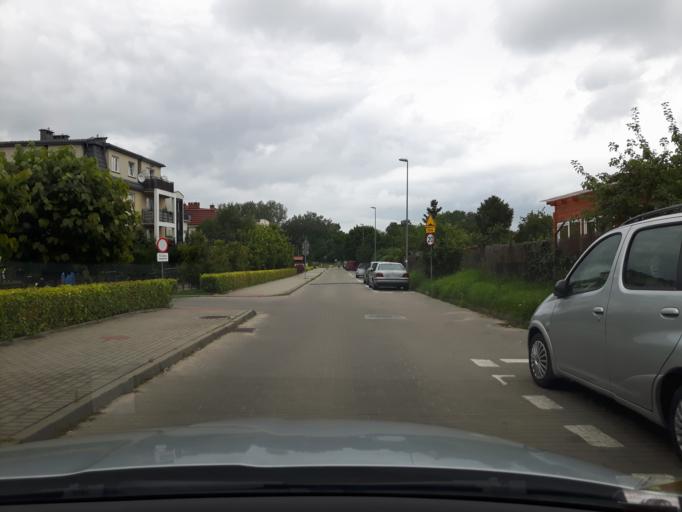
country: PL
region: Pomeranian Voivodeship
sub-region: Sopot
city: Sopot
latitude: 54.4295
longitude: 18.5755
